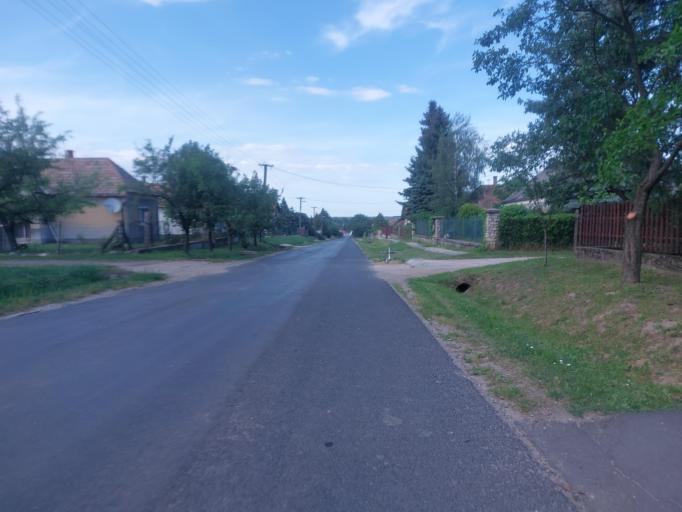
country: HU
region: Veszprem
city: Devecser
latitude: 47.1608
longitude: 17.3757
